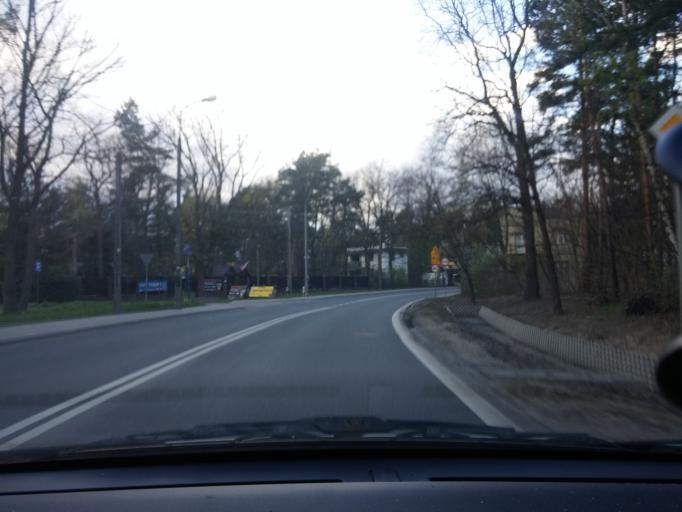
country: PL
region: Masovian Voivodeship
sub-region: Warszawa
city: Wawer
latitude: 52.2108
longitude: 21.1677
